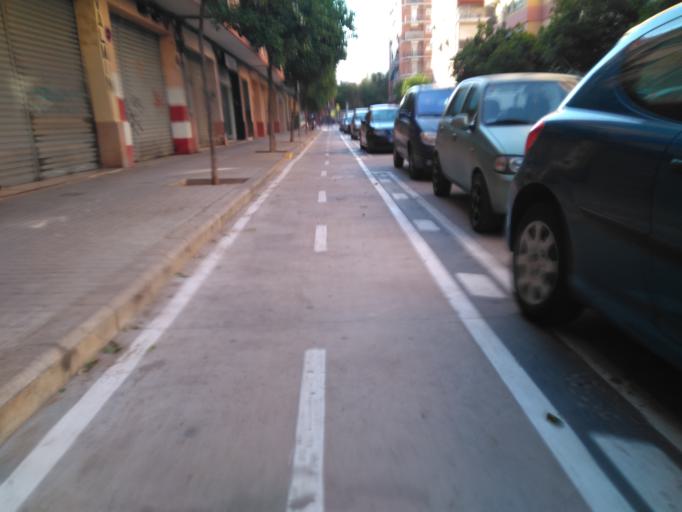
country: ES
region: Valencia
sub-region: Provincia de Valencia
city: Tavernes Blanques
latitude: 39.4905
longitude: -0.3694
